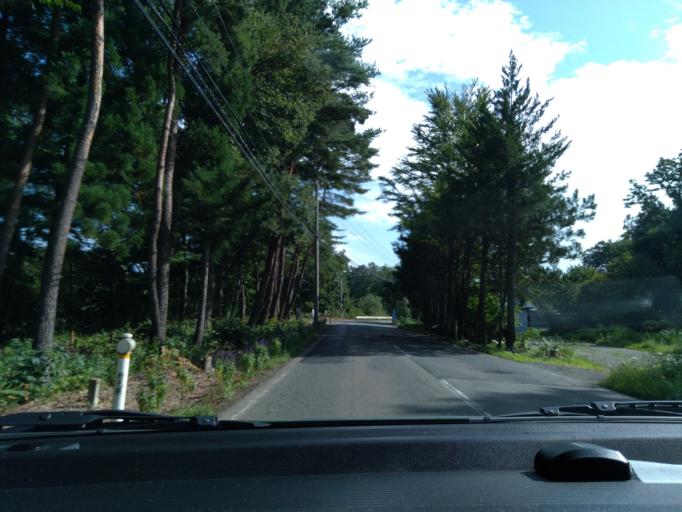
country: JP
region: Iwate
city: Shizukuishi
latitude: 39.6539
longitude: 140.9926
